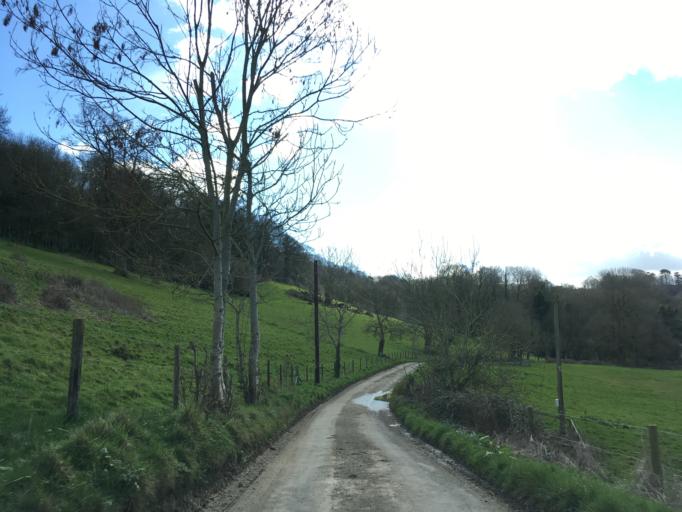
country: GB
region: England
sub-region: South Gloucestershire
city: Horton
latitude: 51.5684
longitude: -2.3383
